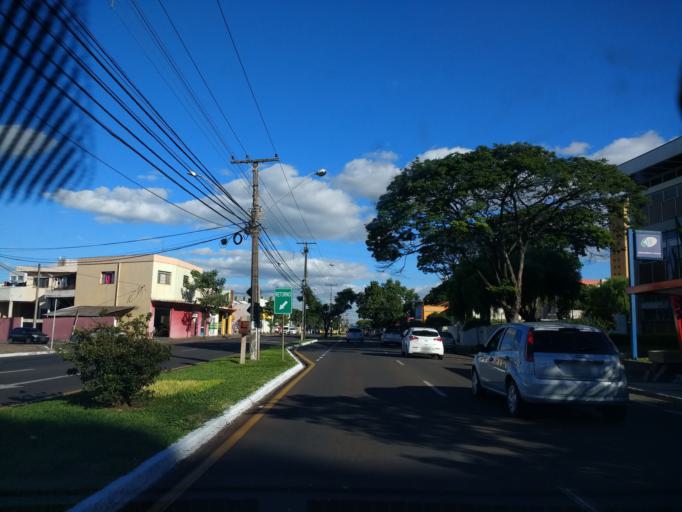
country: BR
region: Parana
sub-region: Londrina
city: Londrina
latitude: -23.3309
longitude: -51.1523
